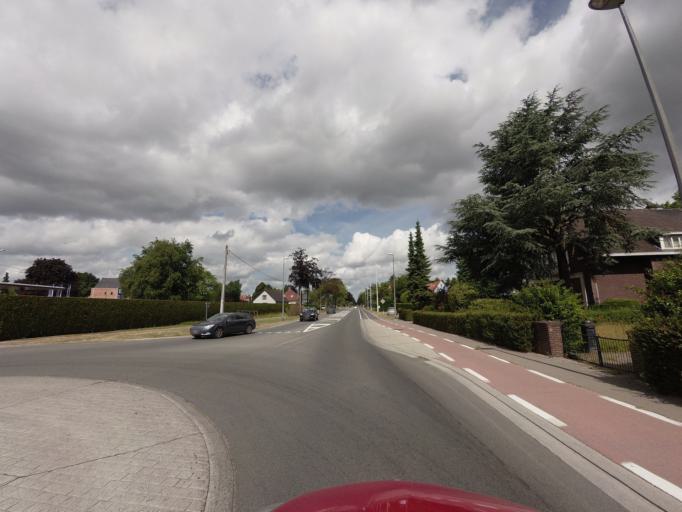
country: BE
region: Flanders
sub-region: Provincie Oost-Vlaanderen
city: Eeklo
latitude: 51.1910
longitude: 3.5535
